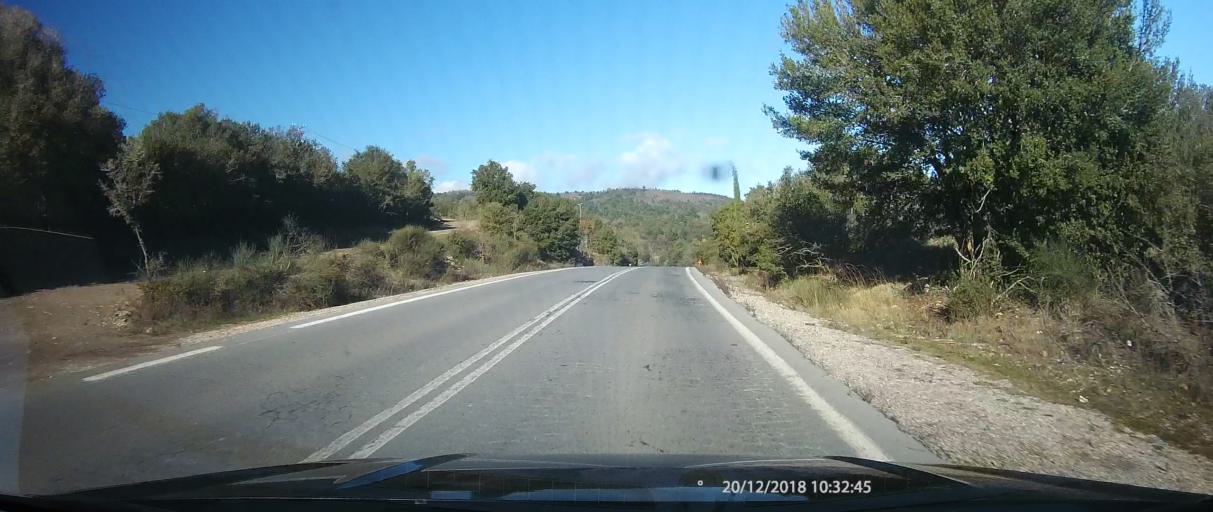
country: GR
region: Peloponnese
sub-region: Nomos Lakonias
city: Kariai
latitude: 37.3302
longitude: 22.4213
